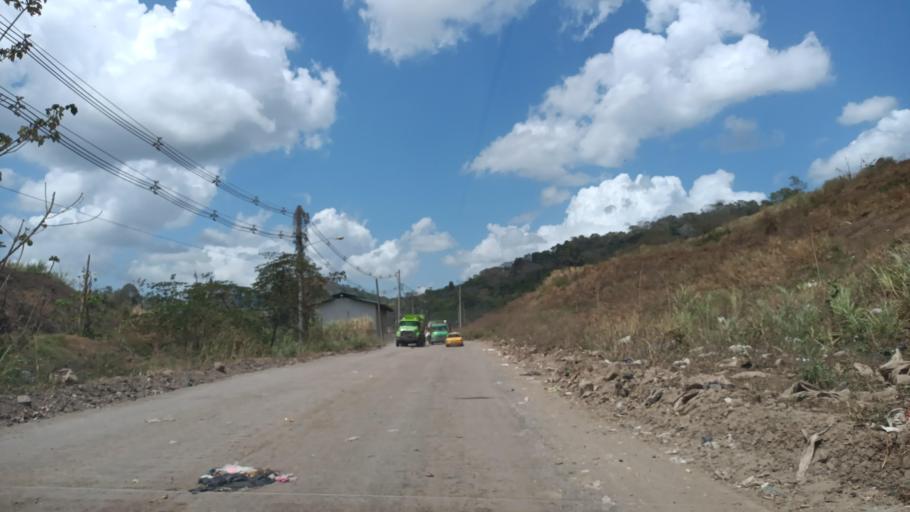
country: PA
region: Panama
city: Las Cumbres
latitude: 9.0535
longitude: -79.5654
